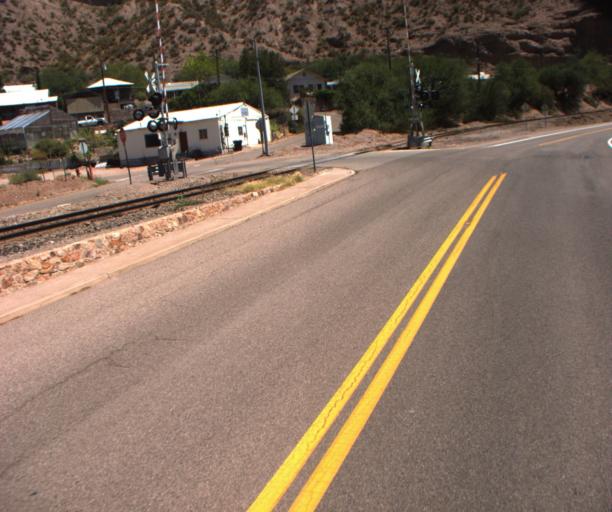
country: US
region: Arizona
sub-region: Greenlee County
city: Clifton
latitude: 33.0443
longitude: -109.2920
